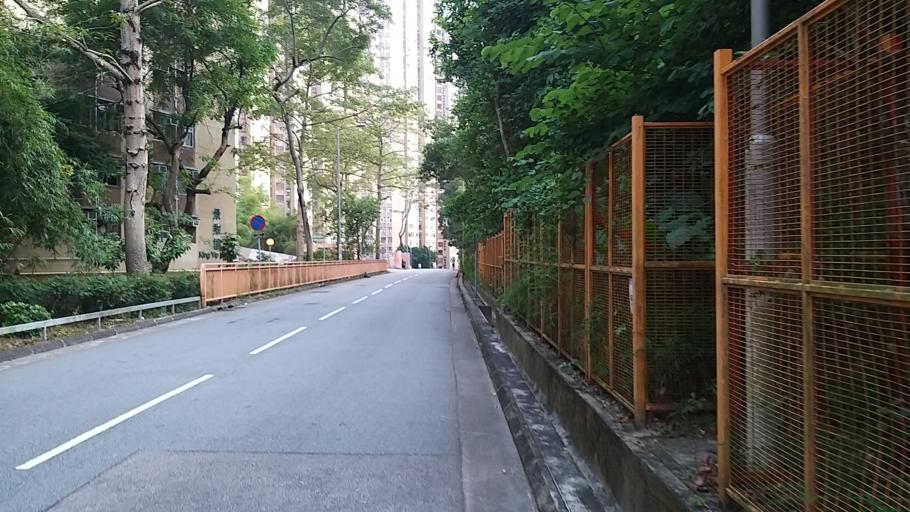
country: HK
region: Tuen Mun
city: Tuen Mun
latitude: 22.3996
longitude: 113.9661
